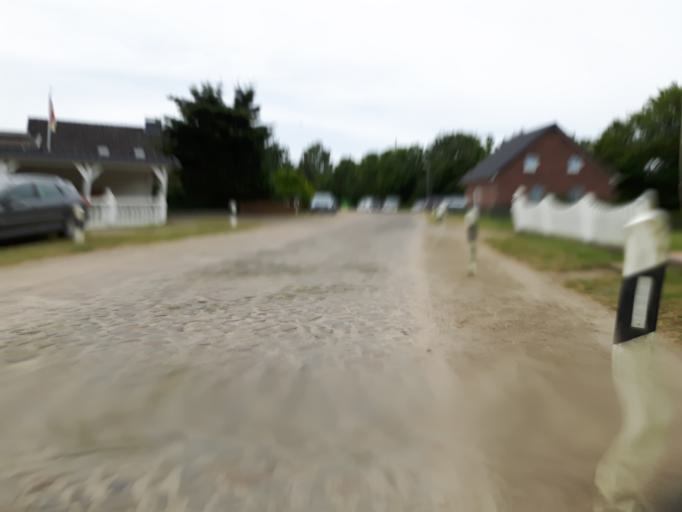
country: DE
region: Lower Saxony
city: Stelle
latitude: 53.3926
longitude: 10.0973
